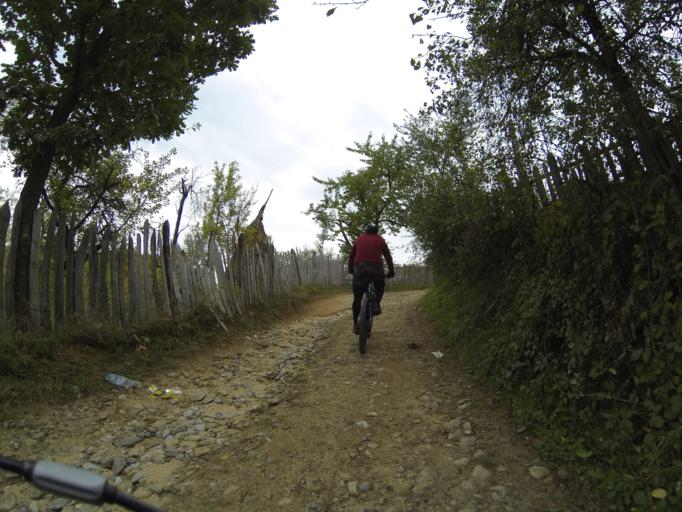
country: RO
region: Gorj
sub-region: Comuna Tismana
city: Sohodol
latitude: 45.0591
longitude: 22.8860
